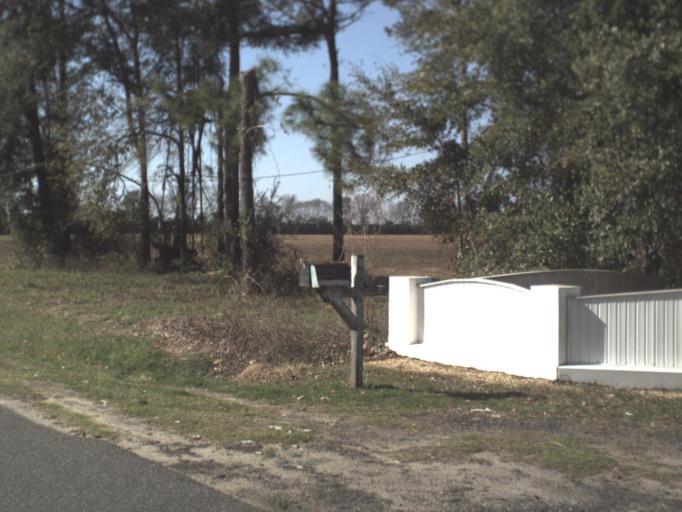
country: US
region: Florida
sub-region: Jackson County
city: Malone
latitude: 30.8590
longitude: -85.1635
